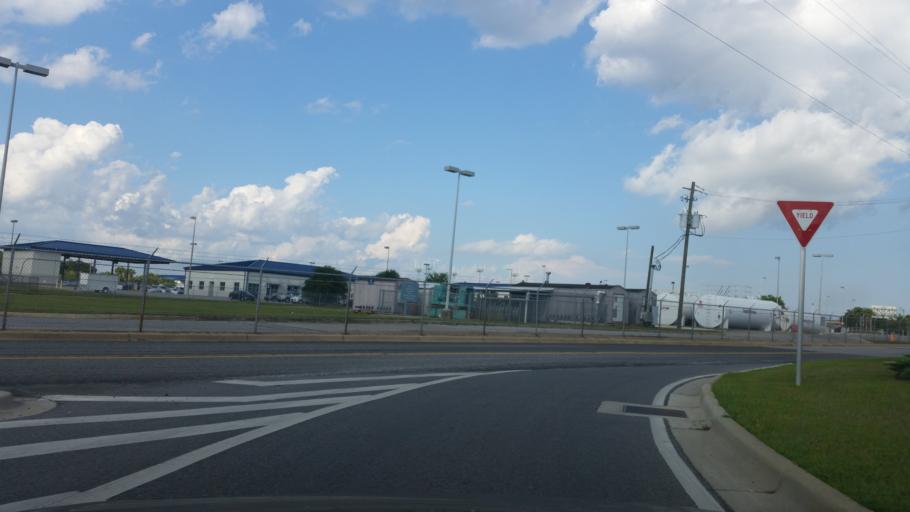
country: US
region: Florida
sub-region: Escambia County
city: Ferry Pass
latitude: 30.4785
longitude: -87.1969
